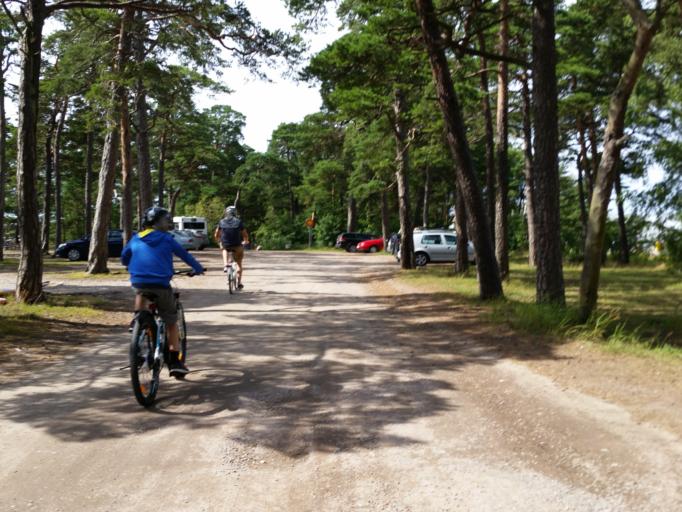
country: FI
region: Uusimaa
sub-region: Raaseporin
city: Hanko
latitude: 59.8246
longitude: 22.9301
